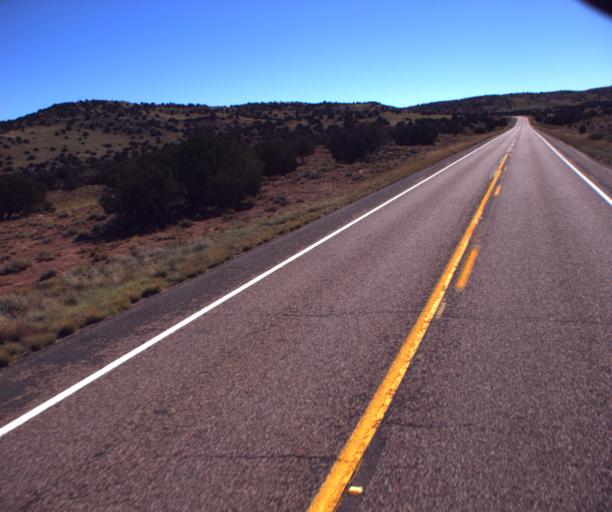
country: US
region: Arizona
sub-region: Apache County
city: Saint Johns
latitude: 34.5789
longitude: -109.5338
